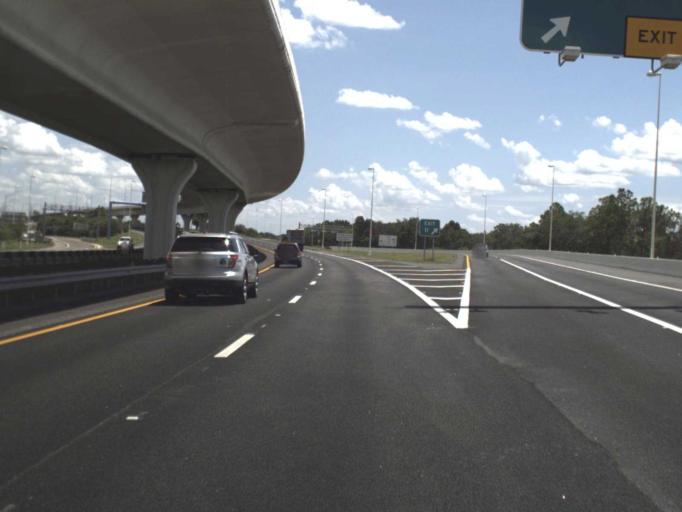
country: US
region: Florida
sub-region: Hillsborough County
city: Palm River-Clair Mel
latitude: 27.9505
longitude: -82.4065
